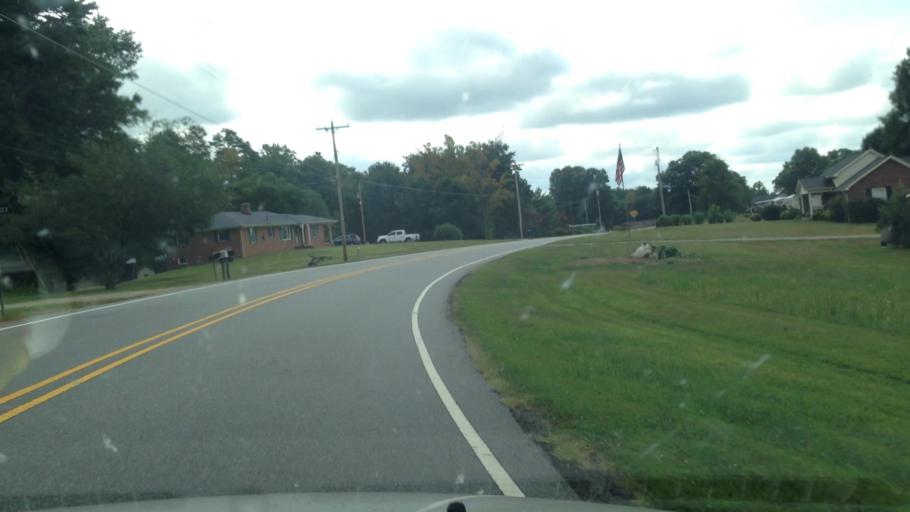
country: US
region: North Carolina
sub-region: Rockingham County
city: Mayodan
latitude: 36.3993
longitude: -80.0335
